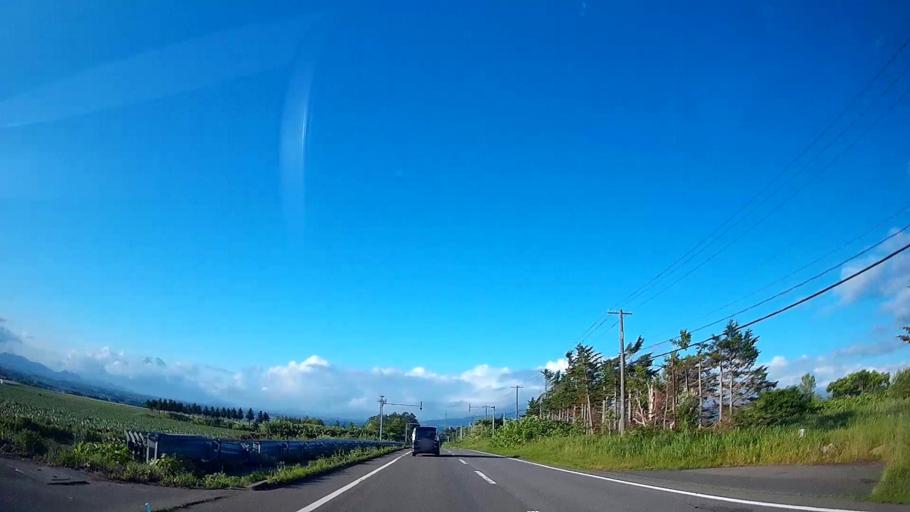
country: JP
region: Hokkaido
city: Date
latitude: 42.6207
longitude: 140.7934
